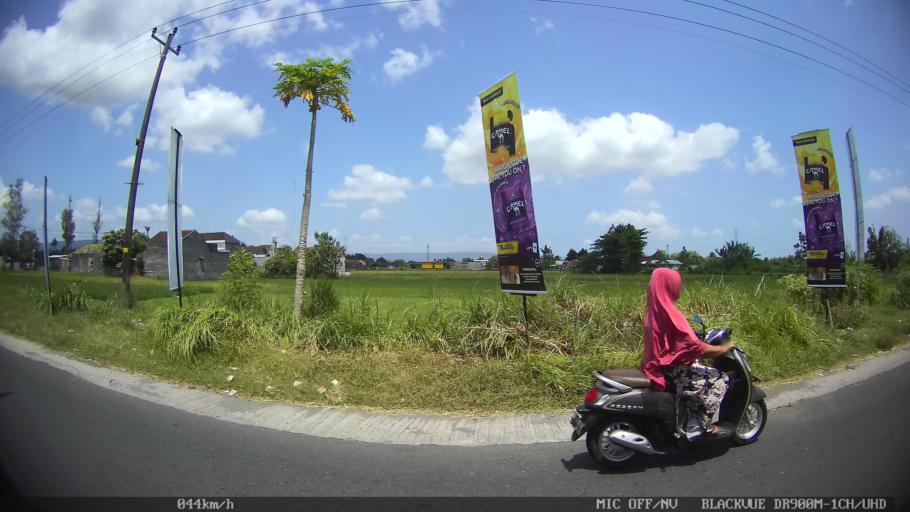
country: ID
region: Daerah Istimewa Yogyakarta
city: Sewon
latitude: -7.8736
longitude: 110.3734
